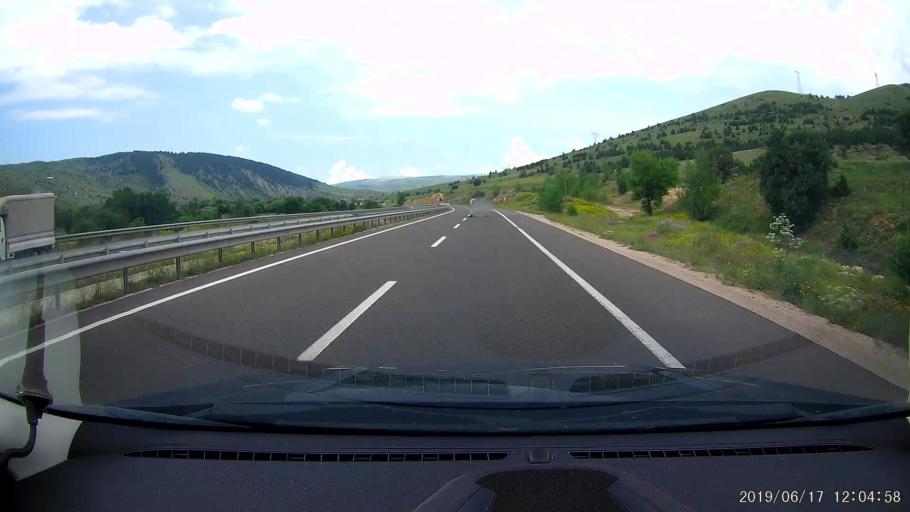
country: TR
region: Cankiri
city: Cerkes
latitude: 40.8276
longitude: 32.7888
